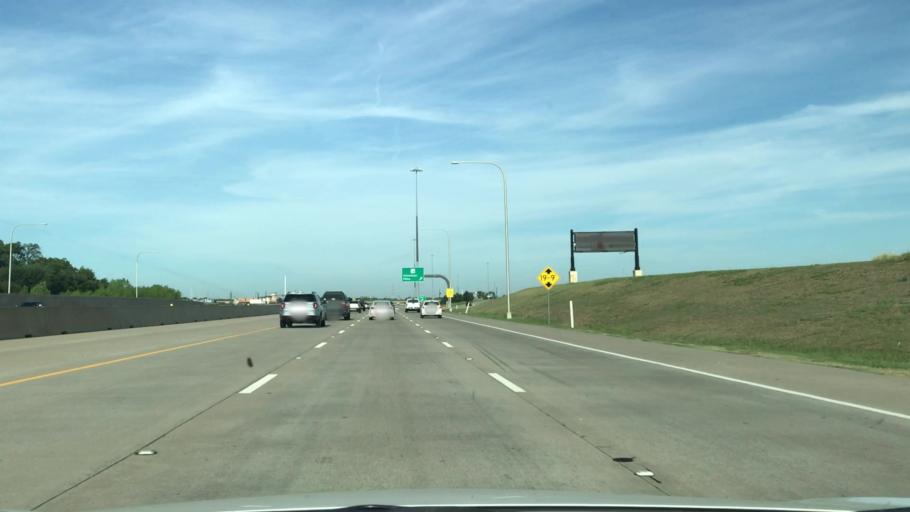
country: US
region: Texas
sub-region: Dallas County
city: Sachse
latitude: 32.9485
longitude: -96.6025
